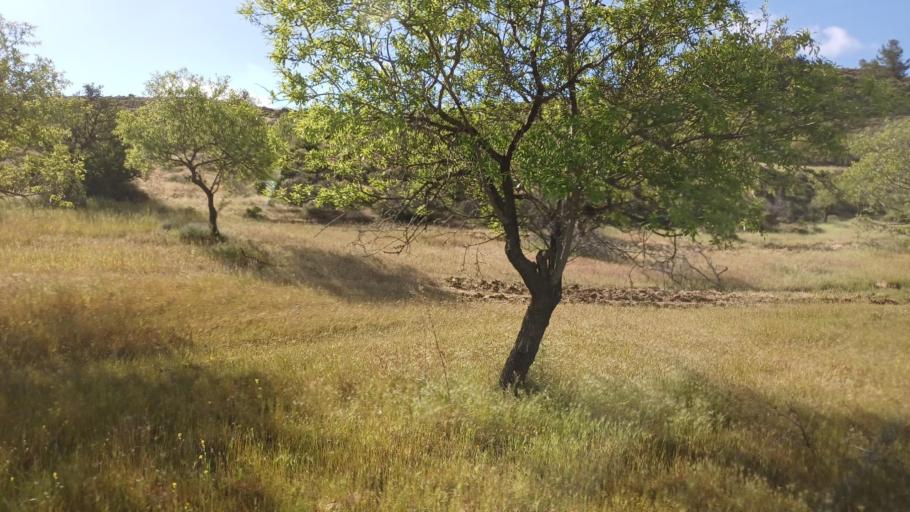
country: CY
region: Lefkosia
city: Peristerona
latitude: 35.0705
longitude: 33.0553
